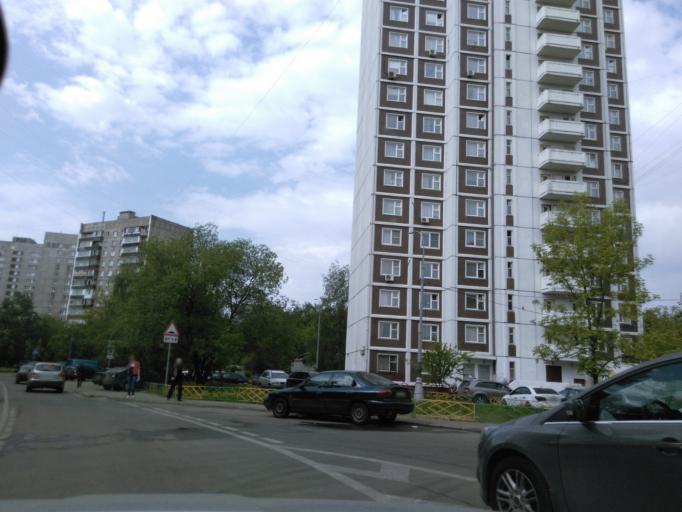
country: RU
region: Moscow
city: Novokhovrino
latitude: 55.8606
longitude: 37.5139
